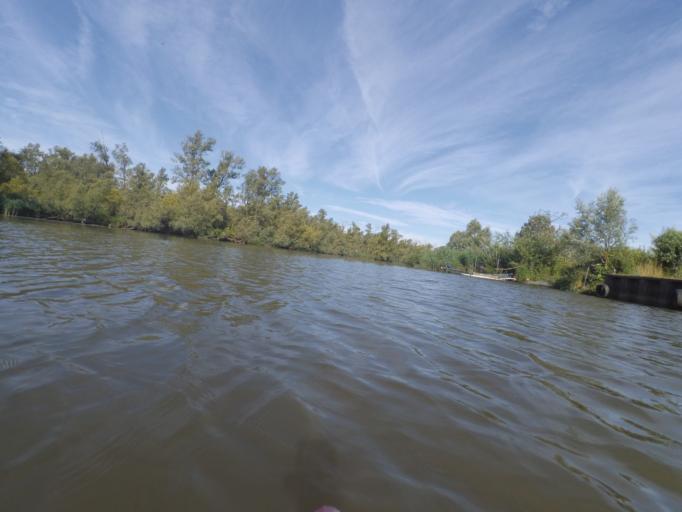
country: NL
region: North Brabant
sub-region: Gemeente Made en Drimmelen
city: Drimmelen
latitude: 51.7335
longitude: 4.8143
